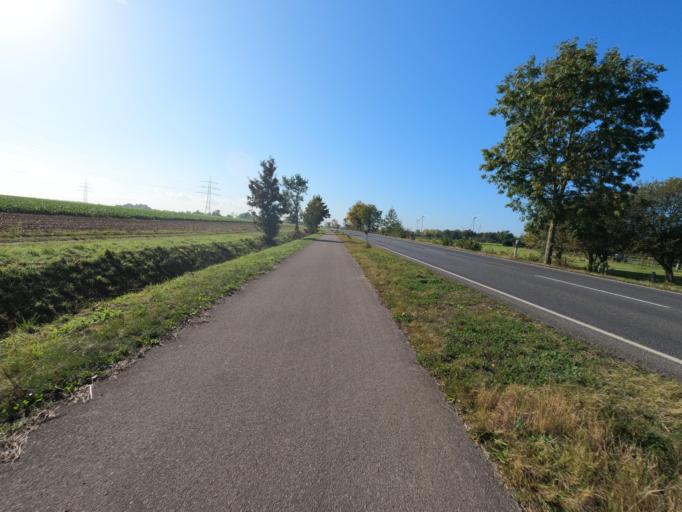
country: DE
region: North Rhine-Westphalia
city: Niedermerz
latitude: 50.8805
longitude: 6.2710
